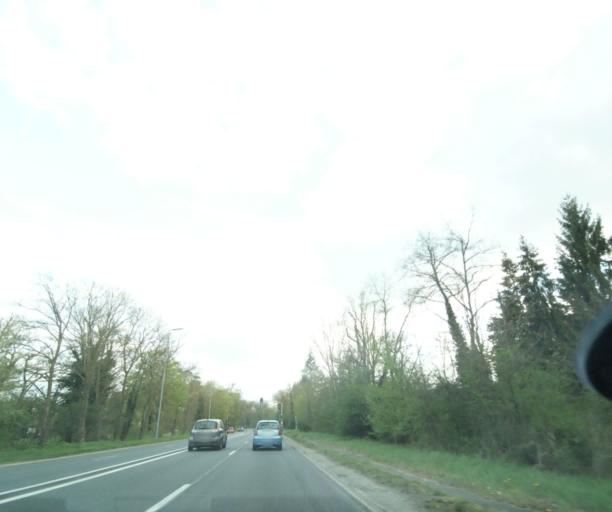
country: FR
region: Ile-de-France
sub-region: Departement de Seine-et-Marne
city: Fontainebleau
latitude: 48.4031
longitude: 2.6870
